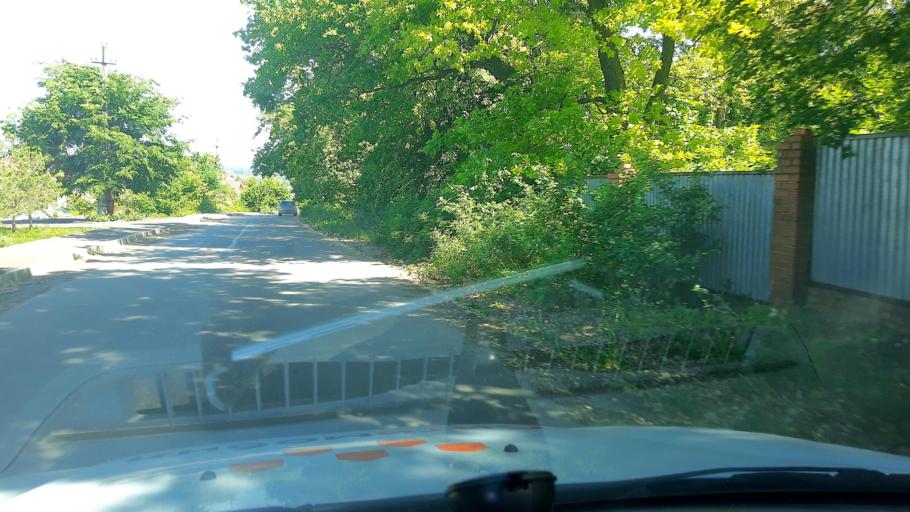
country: RU
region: Bashkortostan
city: Ufa
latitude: 54.6016
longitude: 55.9611
